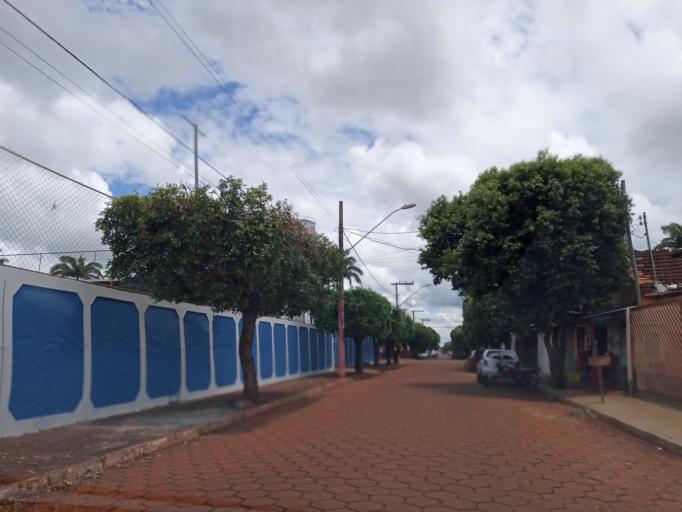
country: BR
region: Minas Gerais
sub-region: Centralina
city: Centralina
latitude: -18.5857
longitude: -49.2006
